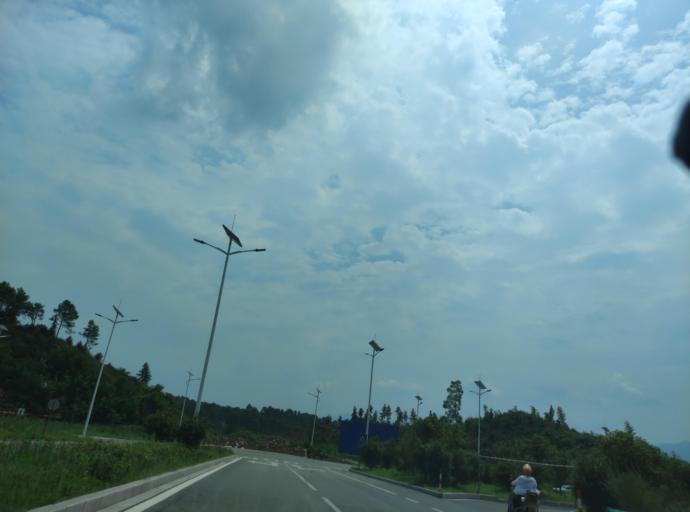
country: CN
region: Jiangxi Sheng
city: Yuannan
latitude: 27.6639
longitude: 114.0391
